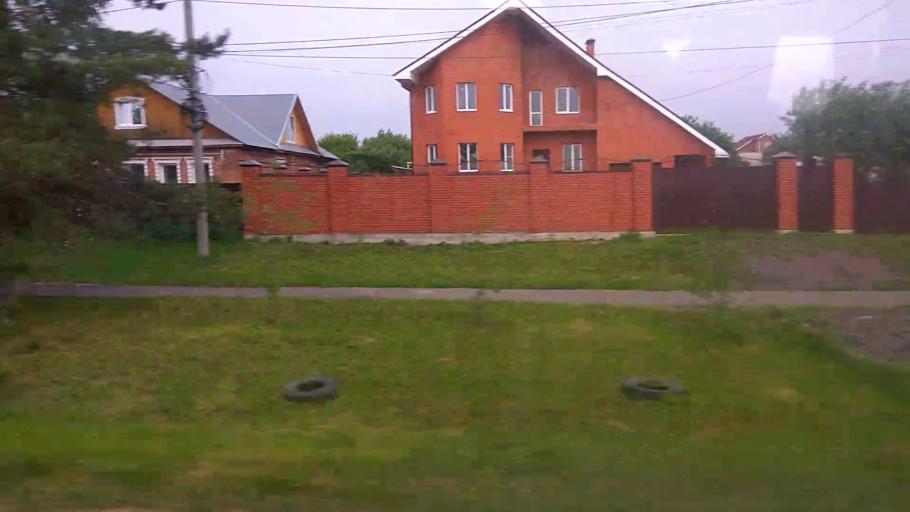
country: RU
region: Moskovskaya
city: Lukhovitsy
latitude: 54.9387
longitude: 39.0145
